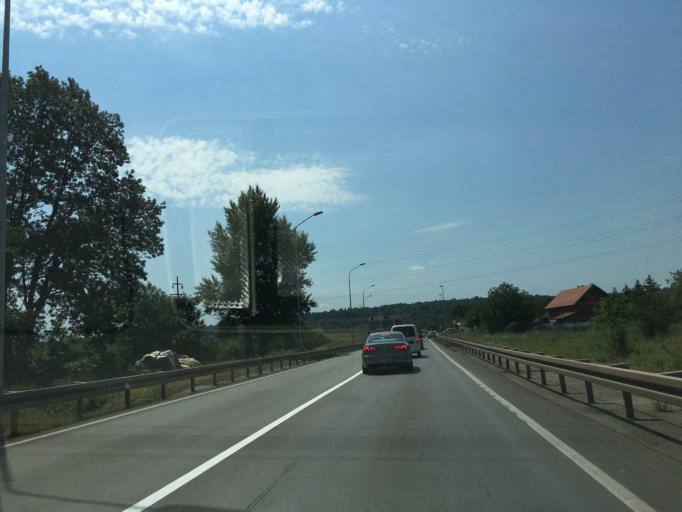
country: RS
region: Central Serbia
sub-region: Podunavski Okrug
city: Smederevo
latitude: 44.5916
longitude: 20.9570
